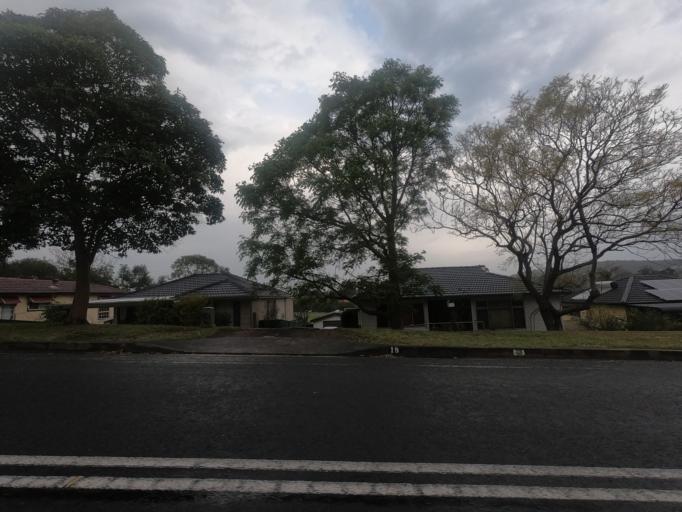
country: AU
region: New South Wales
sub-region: Wollongong
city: Koonawarra
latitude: -34.4951
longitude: 150.8077
